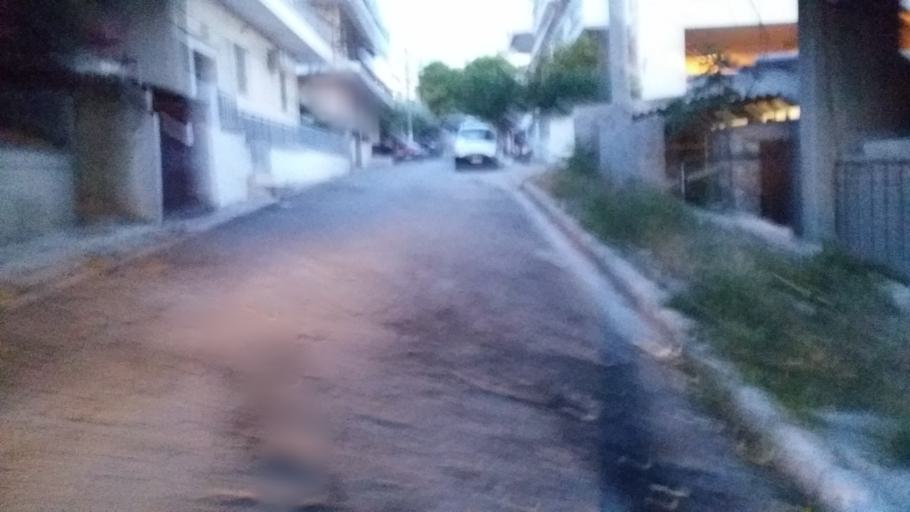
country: GR
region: Attica
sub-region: Nomarchia Athinas
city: Metamorfosi
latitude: 38.0592
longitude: 23.7573
